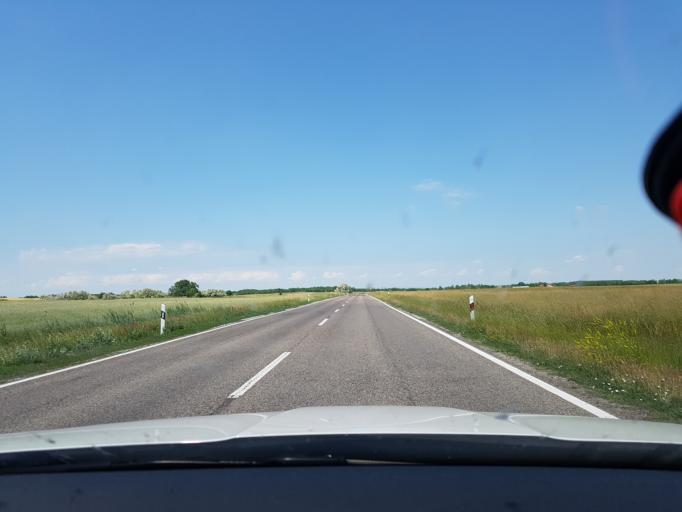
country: HU
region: Hajdu-Bihar
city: Egyek
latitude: 47.5762
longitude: 20.8566
